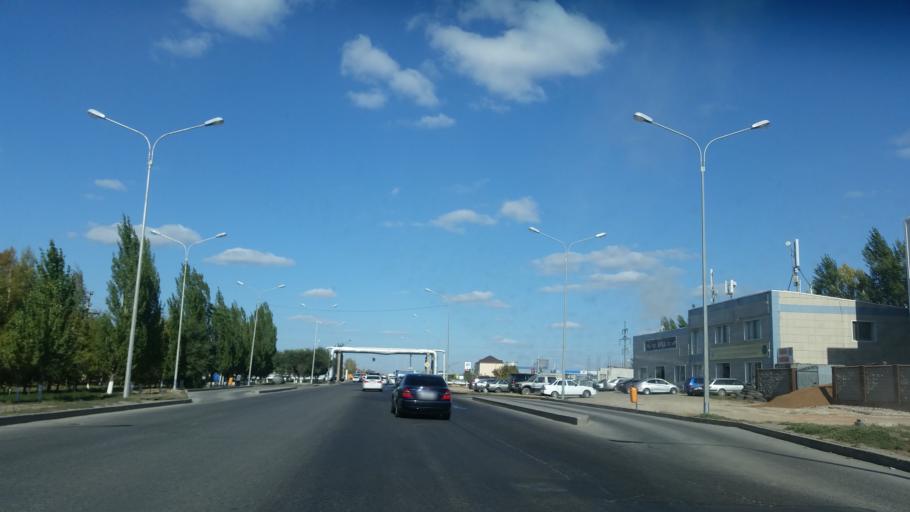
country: KZ
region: Astana Qalasy
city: Astana
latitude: 51.1774
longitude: 71.4870
